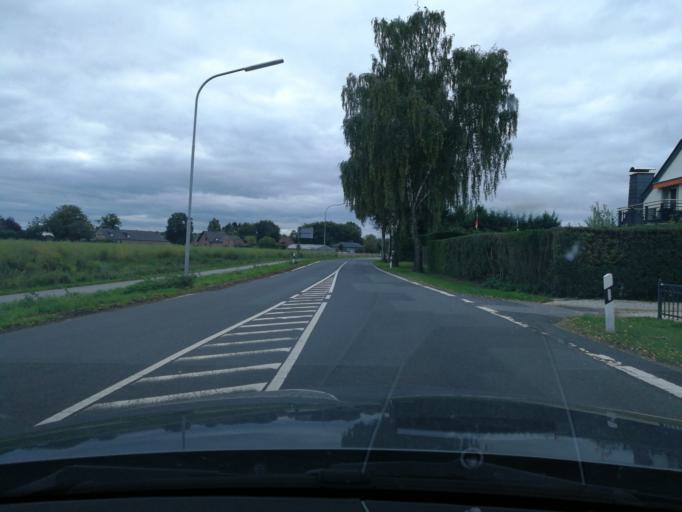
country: NL
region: Limburg
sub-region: Gemeente Venlo
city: Arcen
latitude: 51.4915
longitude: 6.2261
